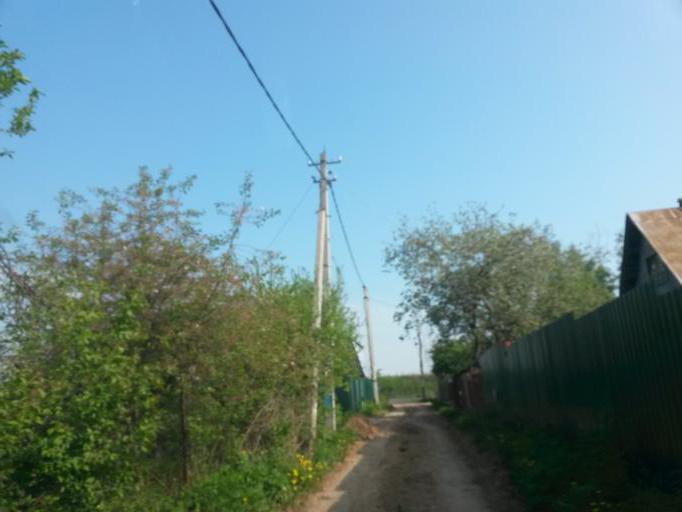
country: RU
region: Moscow
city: Zyablikovo
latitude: 55.5955
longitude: 37.7681
